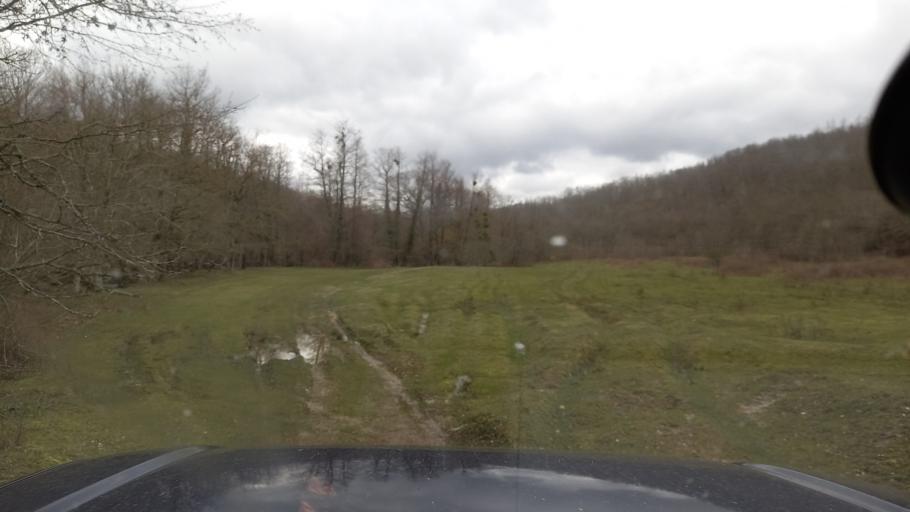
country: RU
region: Krasnodarskiy
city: Pshada
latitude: 44.4837
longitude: 38.4011
